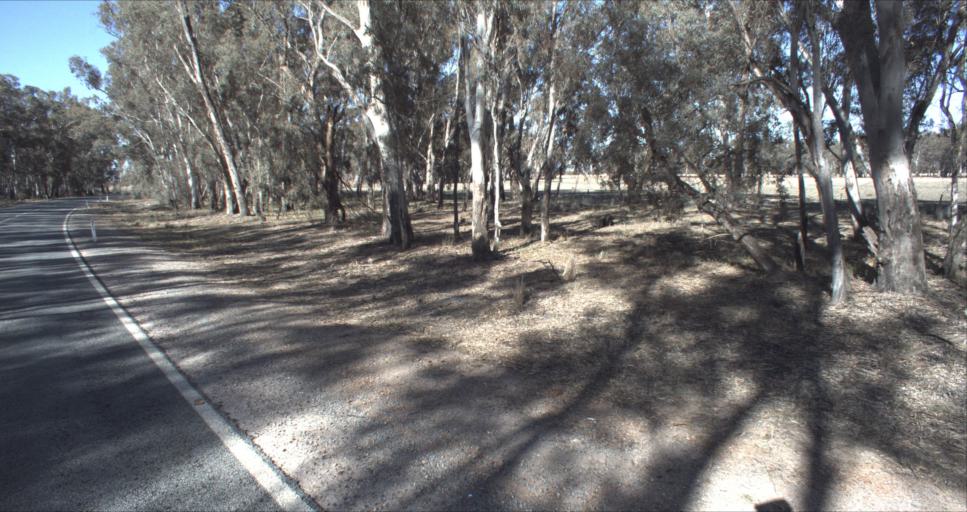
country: AU
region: New South Wales
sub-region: Leeton
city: Leeton
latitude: -34.6254
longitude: 146.3798
